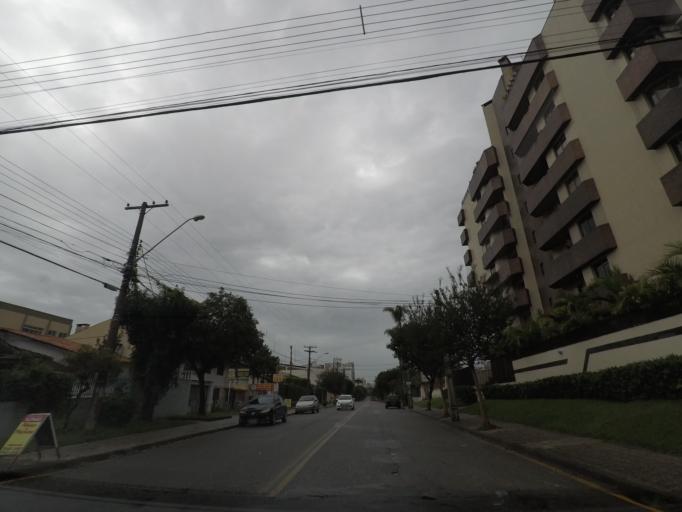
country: BR
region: Parana
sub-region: Curitiba
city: Curitiba
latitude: -25.4603
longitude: -49.2865
